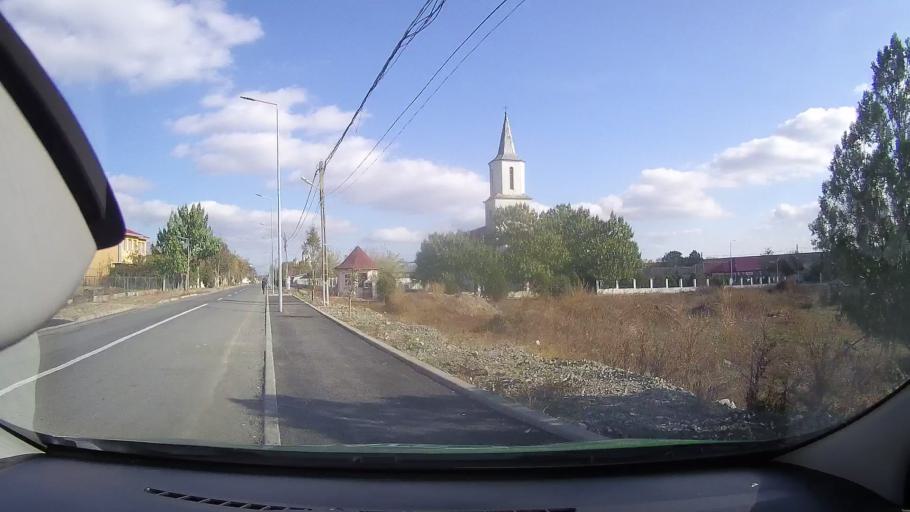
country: RO
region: Constanta
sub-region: Comuna Cogealac
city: Cogealac
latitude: 44.5555
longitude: 28.5609
